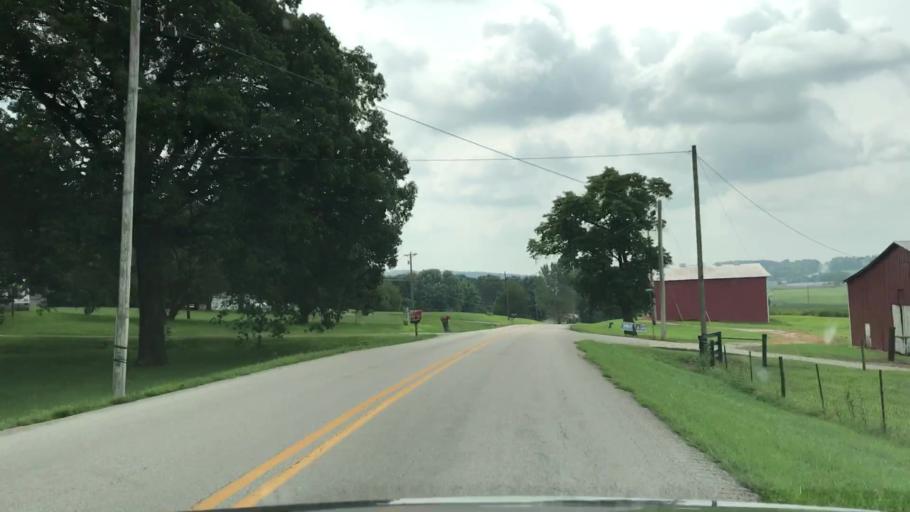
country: US
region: Kentucky
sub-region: Barren County
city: Cave City
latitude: 37.1071
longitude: -85.9814
